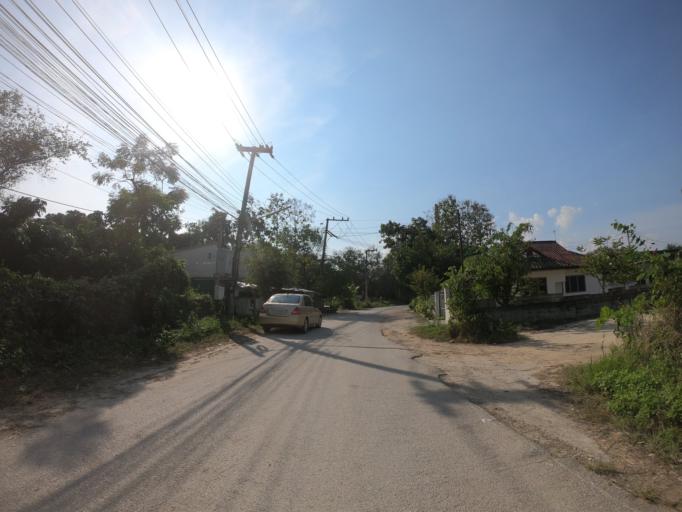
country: TH
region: Chiang Mai
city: Chiang Mai
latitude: 18.8283
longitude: 99.0001
